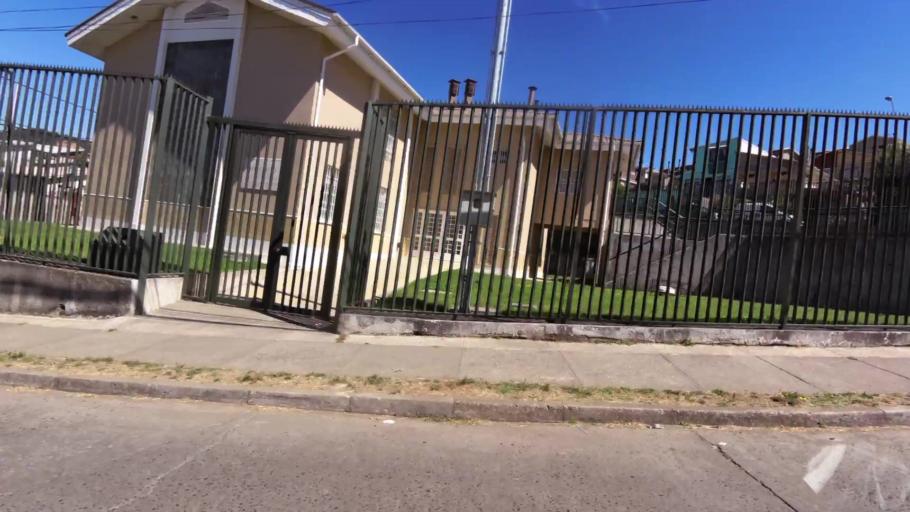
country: CL
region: Biobio
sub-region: Provincia de Concepcion
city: Penco
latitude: -36.7272
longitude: -72.9847
